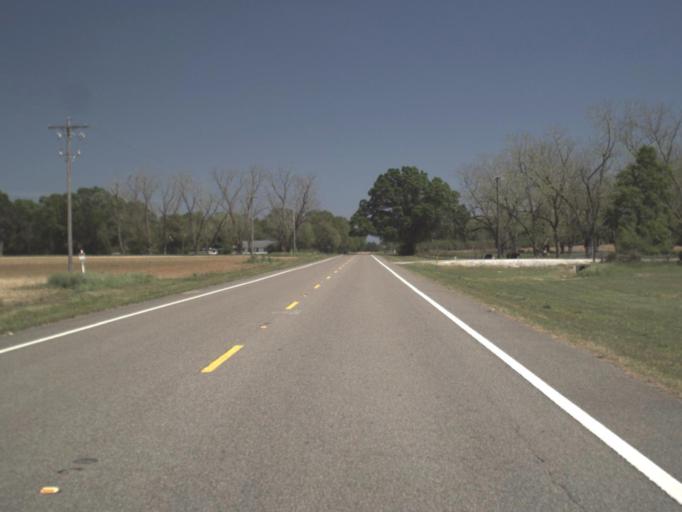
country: US
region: Alabama
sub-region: Escambia County
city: East Brewton
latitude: 30.8995
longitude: -87.0088
